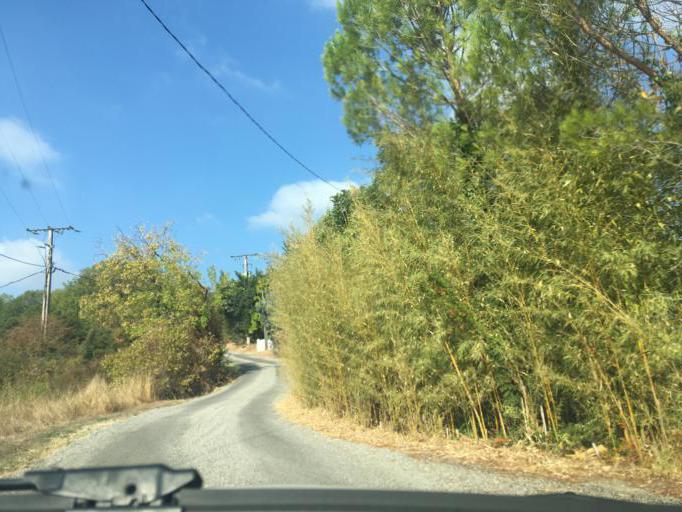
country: FR
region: Provence-Alpes-Cote d'Azur
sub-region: Departement du Var
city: Lorgues
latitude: 43.4872
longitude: 6.3996
